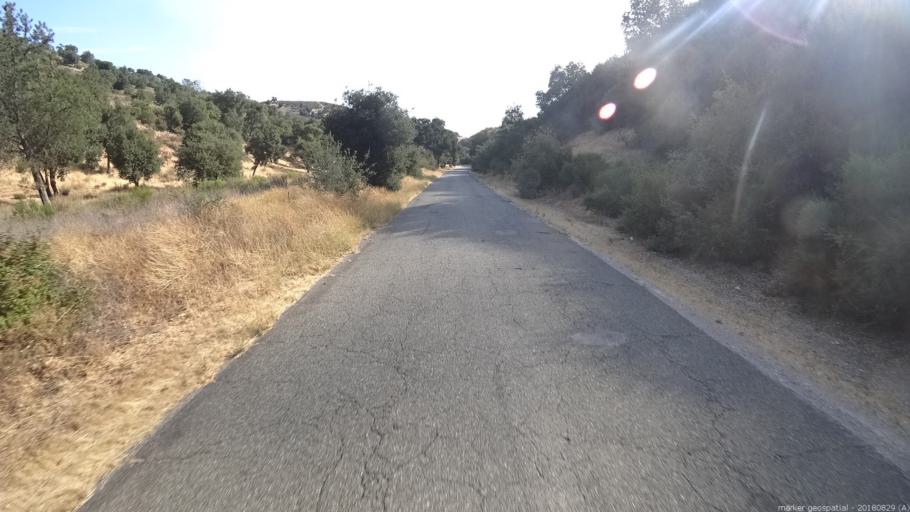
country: US
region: California
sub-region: Monterey County
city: King City
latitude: 36.0417
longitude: -121.0777
